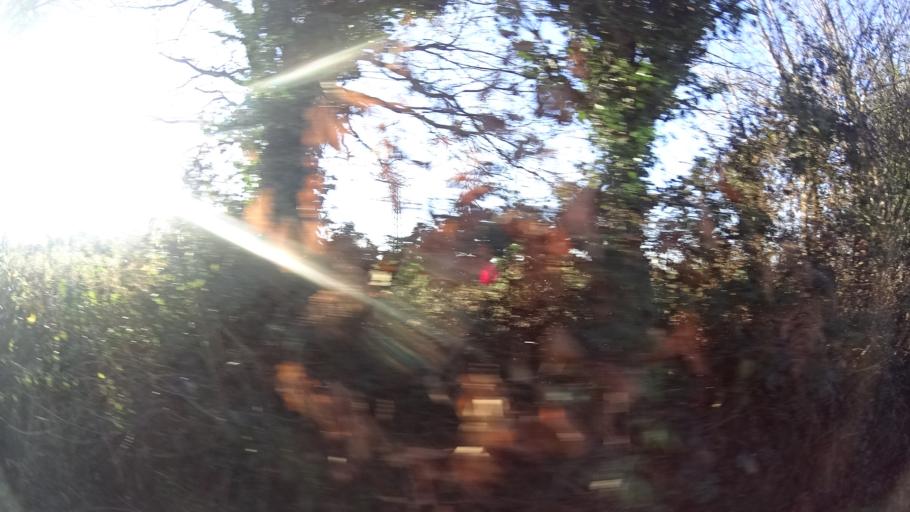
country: FR
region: Brittany
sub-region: Departement du Morbihan
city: Saint-Jacut-les-Pins
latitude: 47.6713
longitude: -2.1946
